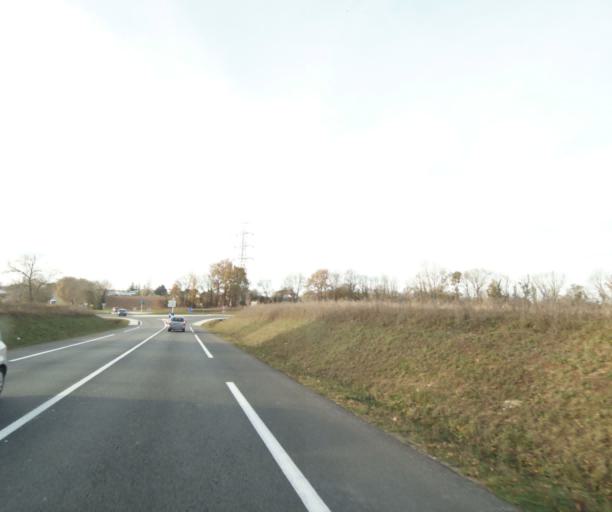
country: FR
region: Poitou-Charentes
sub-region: Departement de la Charente-Maritime
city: Fontcouverte
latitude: 45.7457
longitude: -0.5882
